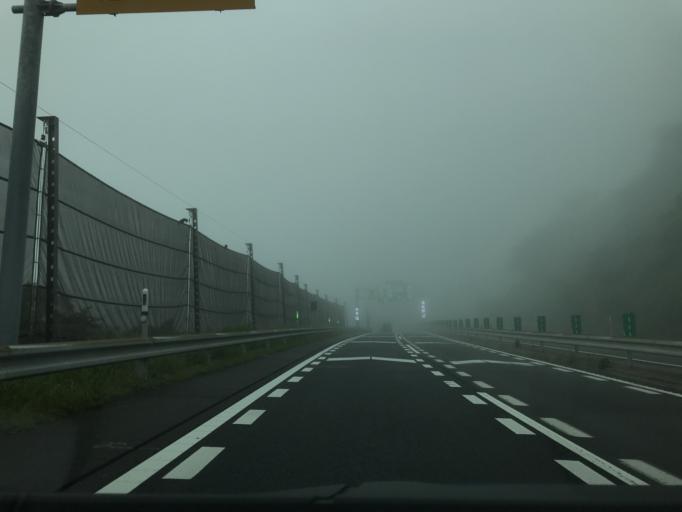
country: JP
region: Oita
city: Hiji
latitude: 33.3581
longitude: 131.4491
